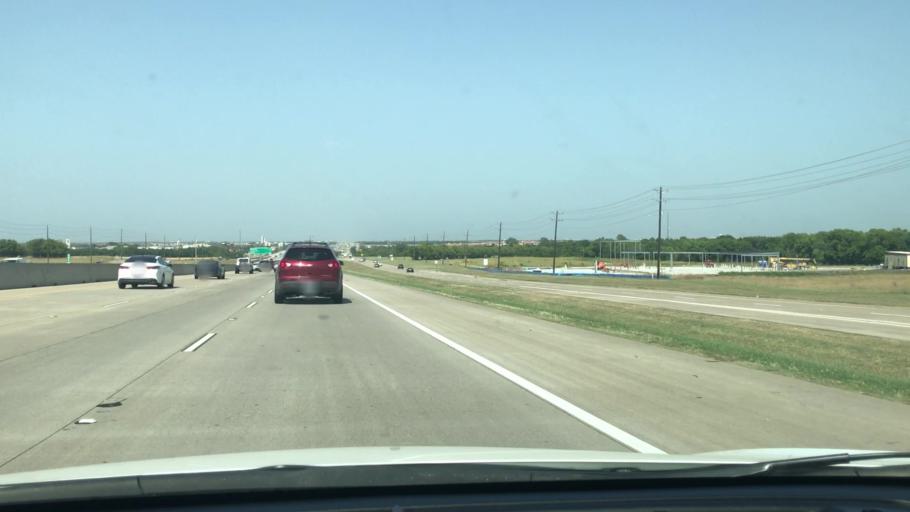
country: US
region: Texas
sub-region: Collin County
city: Frisco
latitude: 33.1143
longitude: -96.7626
